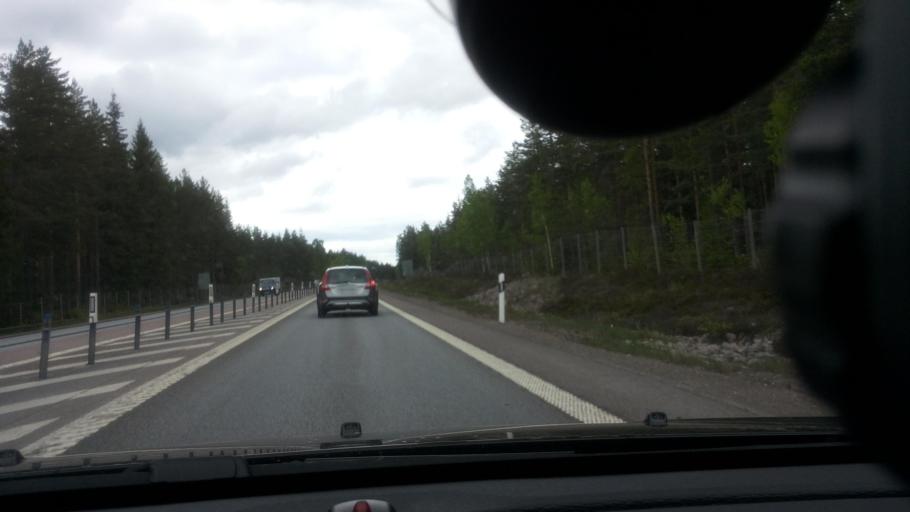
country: SE
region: Gaevleborg
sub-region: Gavle Kommun
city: Norrsundet
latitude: 60.8716
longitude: 17.0515
